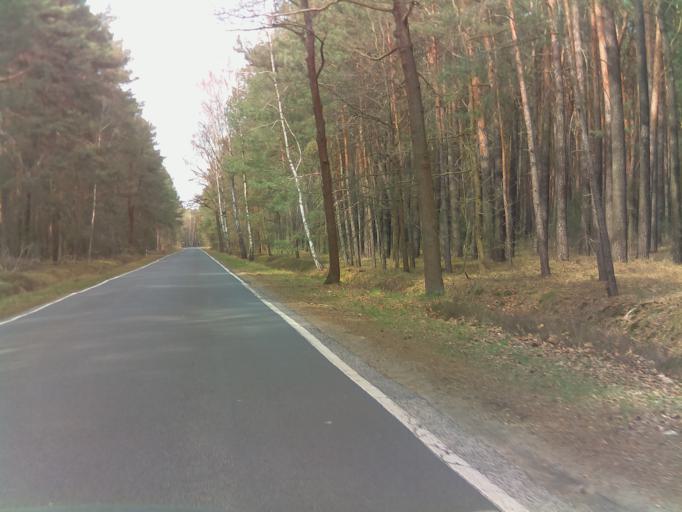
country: DE
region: Brandenburg
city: Cottbus
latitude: 51.7918
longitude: 14.3376
